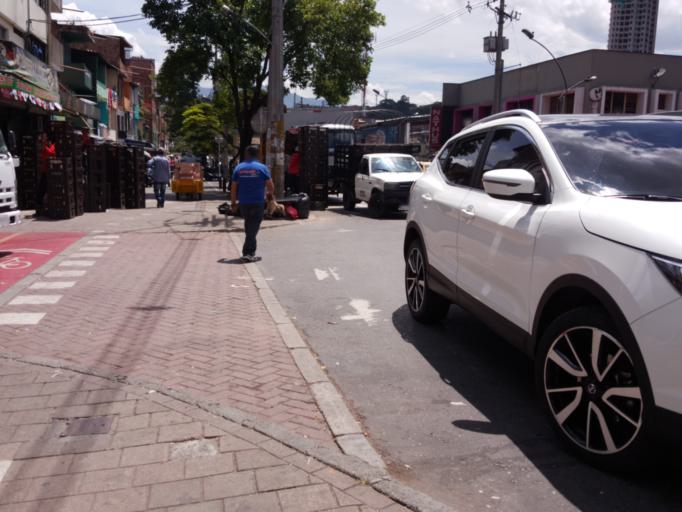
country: CO
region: Antioquia
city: Medellin
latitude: 6.2737
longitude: -75.5648
